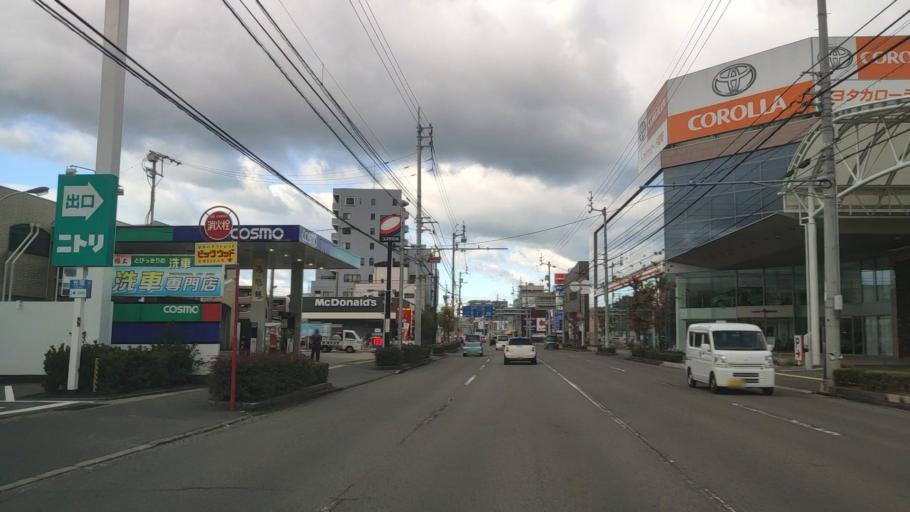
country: JP
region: Ehime
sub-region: Shikoku-chuo Shi
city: Matsuyama
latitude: 33.8546
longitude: 132.7503
